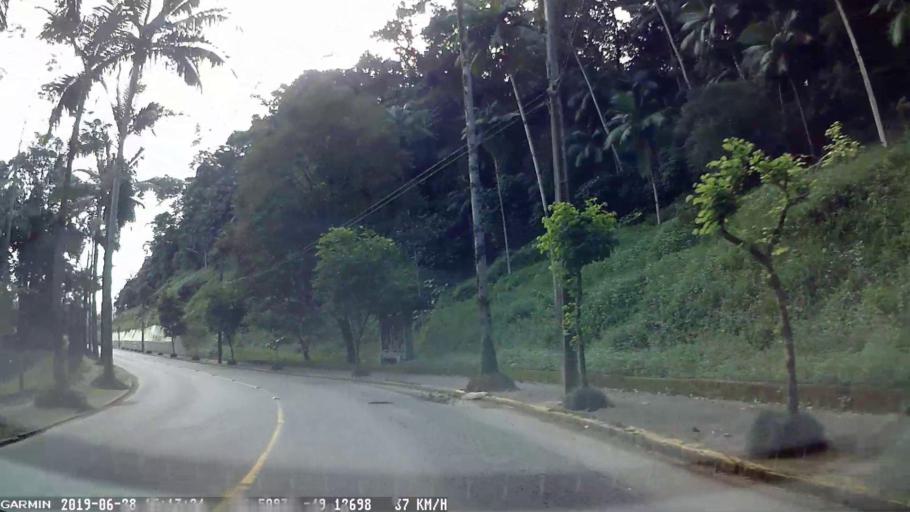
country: BR
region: Santa Catarina
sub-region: Jaragua Do Sul
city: Jaragua do Sul
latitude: -26.5092
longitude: -49.1271
